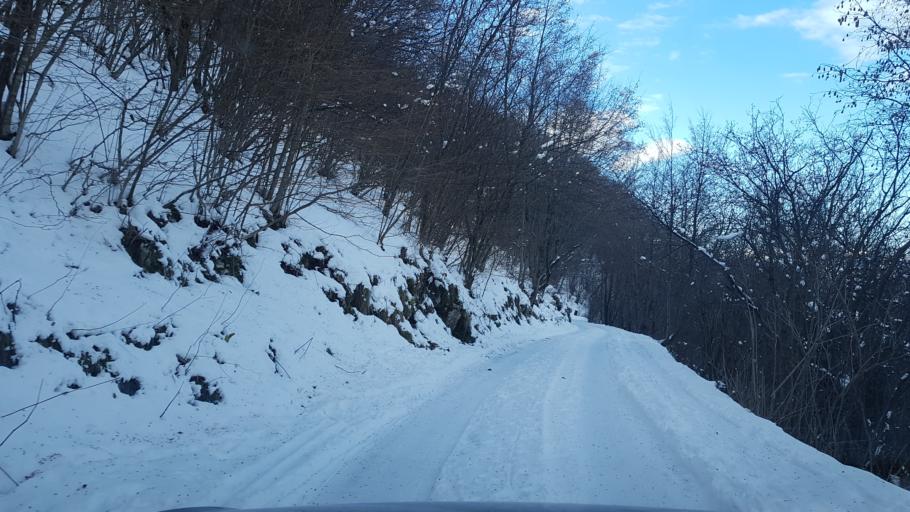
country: IT
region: Friuli Venezia Giulia
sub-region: Provincia di Udine
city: Montenars
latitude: 46.2751
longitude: 13.1624
